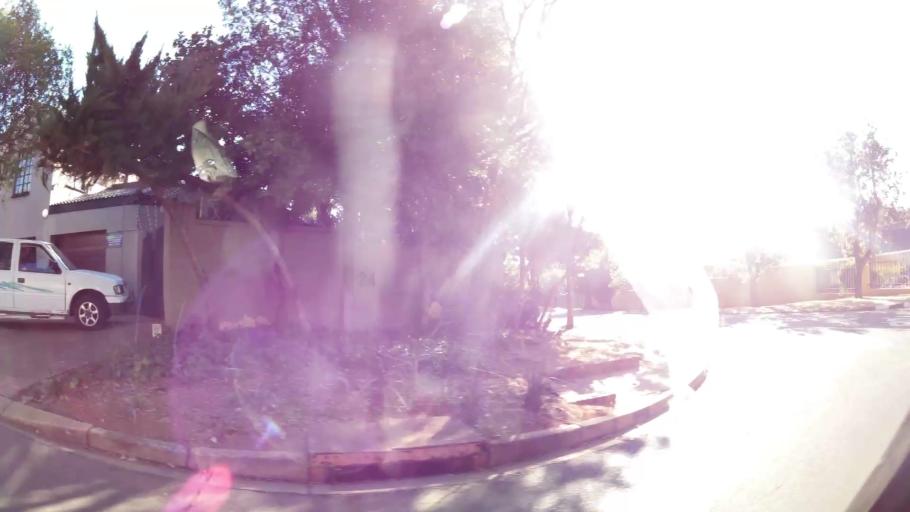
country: ZA
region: Gauteng
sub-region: City of Johannesburg Metropolitan Municipality
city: Roodepoort
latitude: -26.0894
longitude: 27.9505
